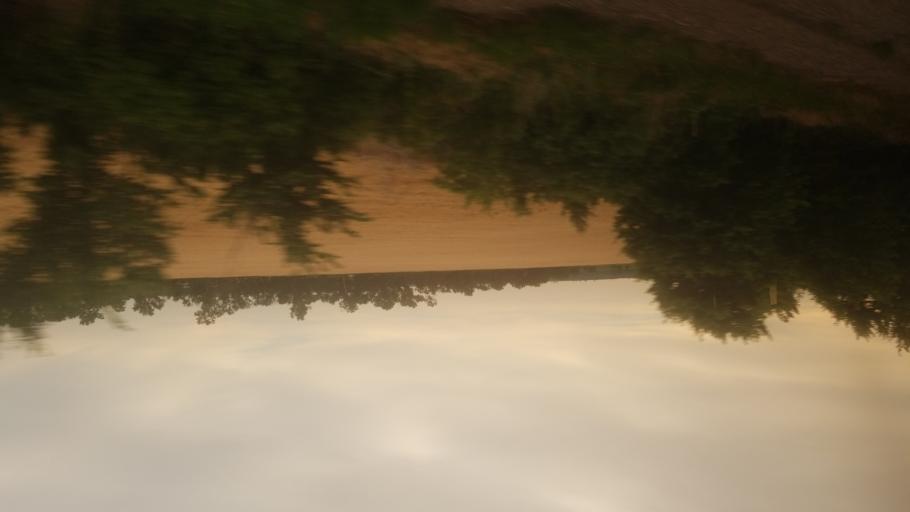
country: US
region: Kansas
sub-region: Chase County
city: Cottonwood Falls
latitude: 38.3867
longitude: -96.4743
